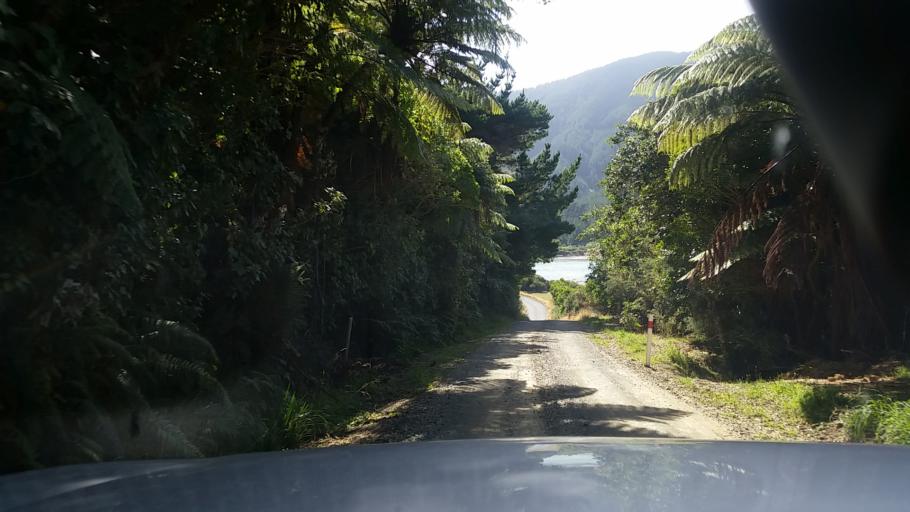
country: NZ
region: Marlborough
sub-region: Marlborough District
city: Picton
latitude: -41.2873
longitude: 174.1761
